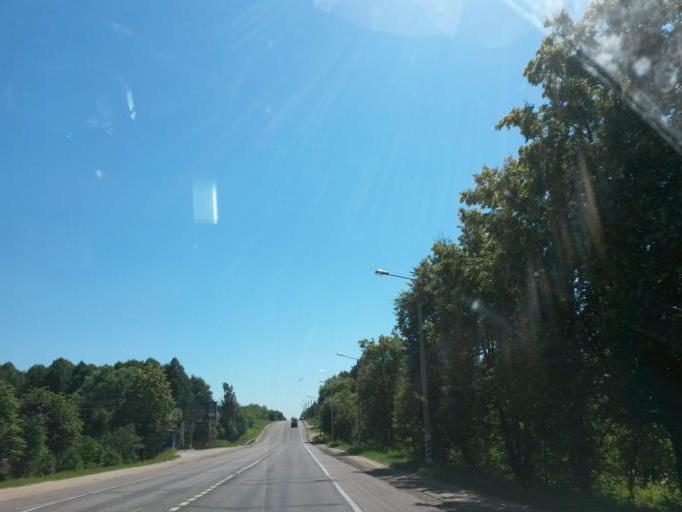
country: RU
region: Moskovskaya
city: Proletarskiy
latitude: 55.0691
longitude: 37.4370
